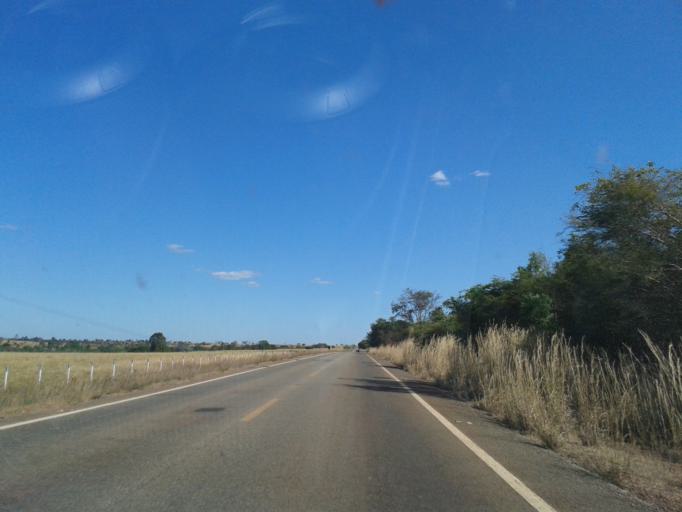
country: BR
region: Goias
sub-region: Mozarlandia
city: Mozarlandia
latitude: -14.3656
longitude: -50.4285
